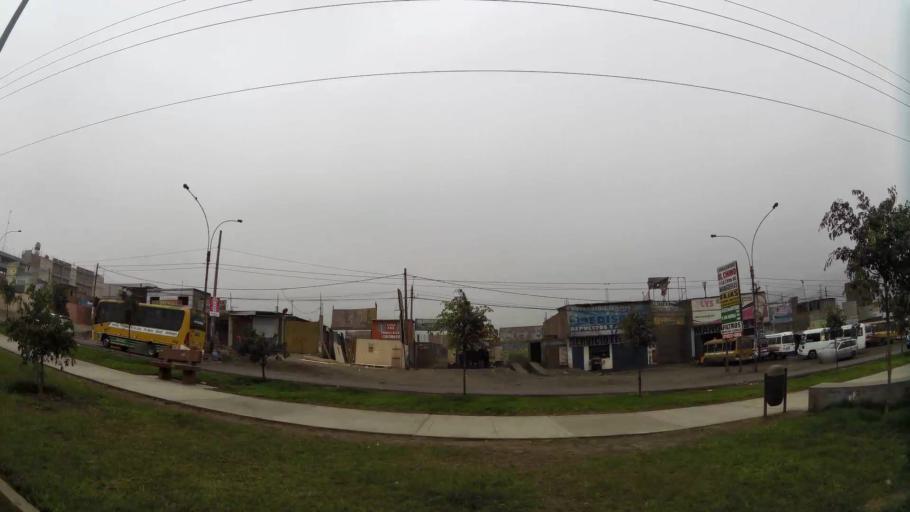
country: PE
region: Lima
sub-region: Lima
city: Urb. Santo Domingo
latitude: -11.9300
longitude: -76.9668
